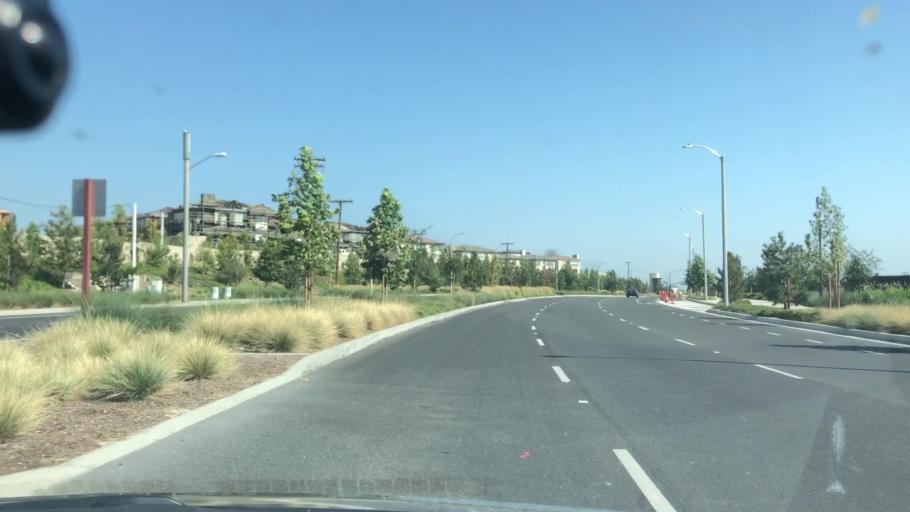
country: US
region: California
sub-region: Orange County
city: Lake Forest
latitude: 33.6830
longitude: -117.7166
